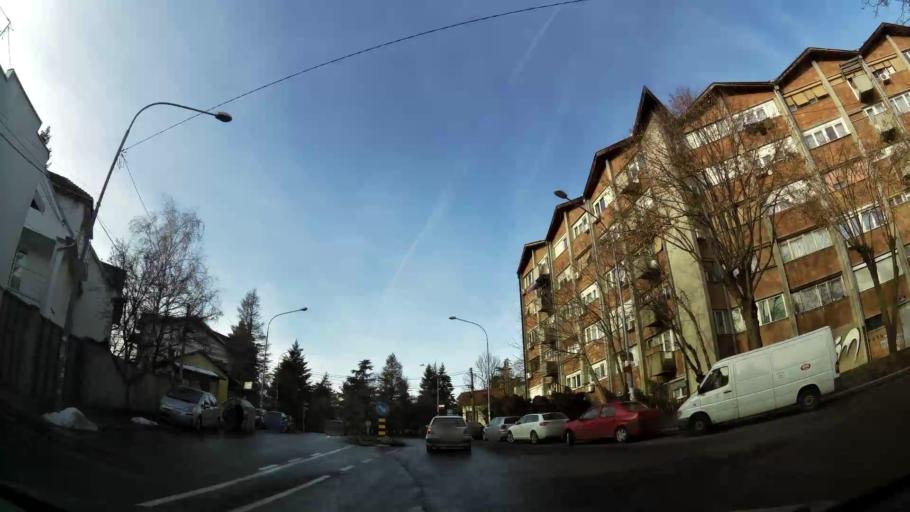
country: RS
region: Central Serbia
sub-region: Belgrade
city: Rakovica
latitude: 44.7522
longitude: 20.4509
